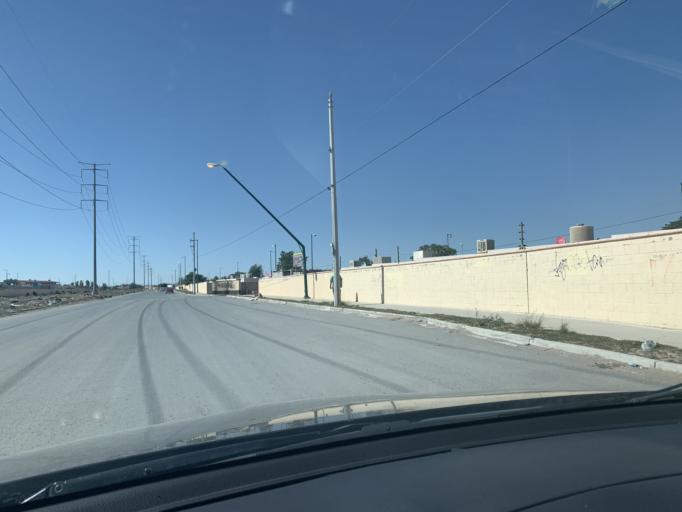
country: US
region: Texas
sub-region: El Paso County
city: Socorro Mission Number 1 Colonia
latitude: 31.5922
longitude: -106.3499
